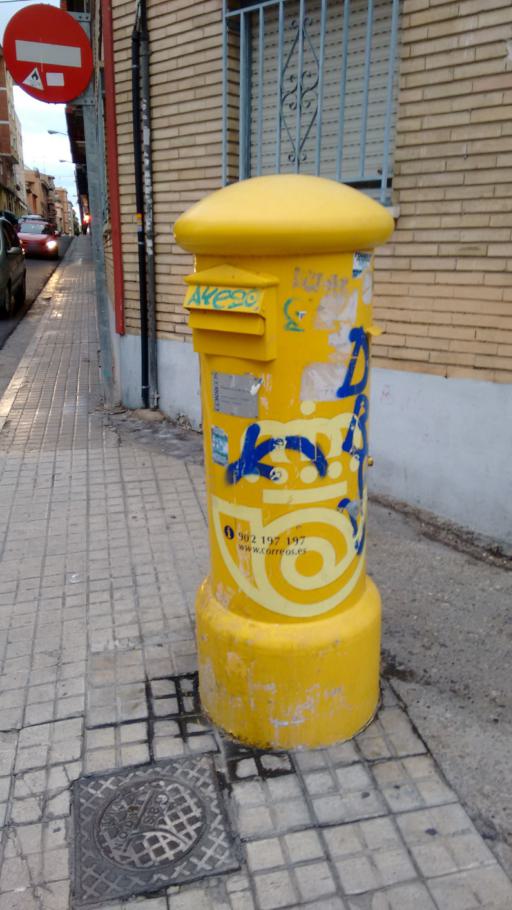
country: ES
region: Aragon
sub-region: Provincia de Zaragoza
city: Delicias
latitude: 41.6299
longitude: -0.8904
